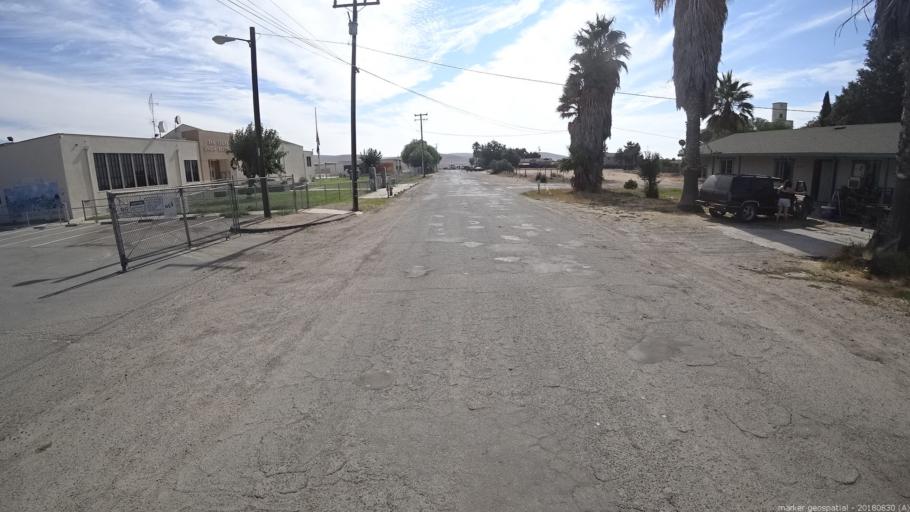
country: US
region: California
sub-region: Monterey County
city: King City
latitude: 36.1294
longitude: -121.0175
